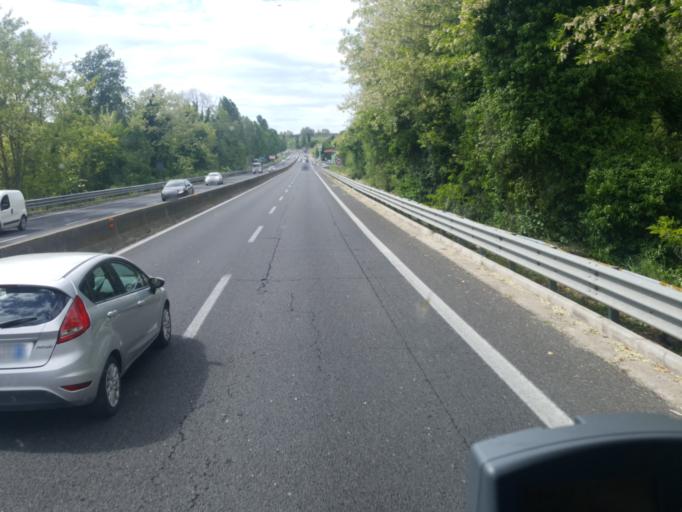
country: IT
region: Latium
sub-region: Citta metropolitana di Roma Capitale
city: Valle Santa
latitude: 41.8902
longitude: 12.2991
